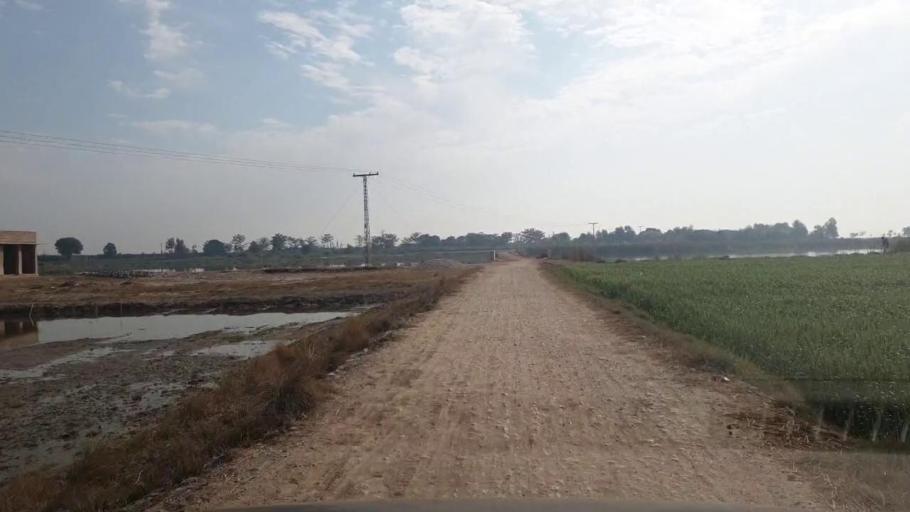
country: PK
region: Sindh
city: Hala
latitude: 25.9916
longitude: 68.4372
